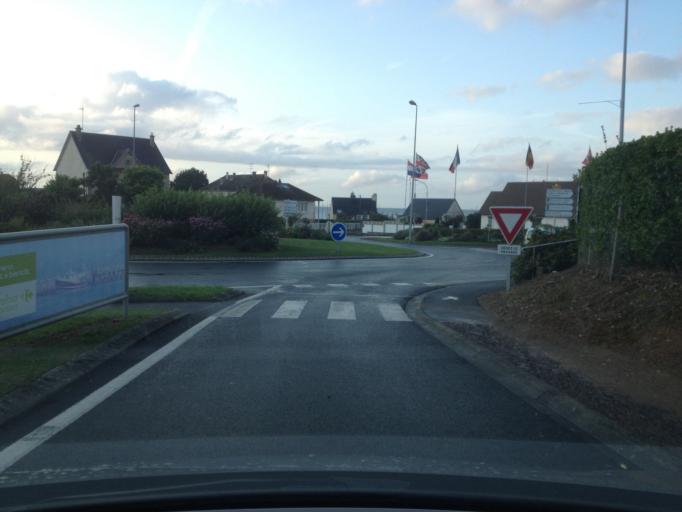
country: FR
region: Lower Normandy
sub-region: Departement du Calvados
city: Grandcamp-Maisy
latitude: 49.3856
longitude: -1.0500
